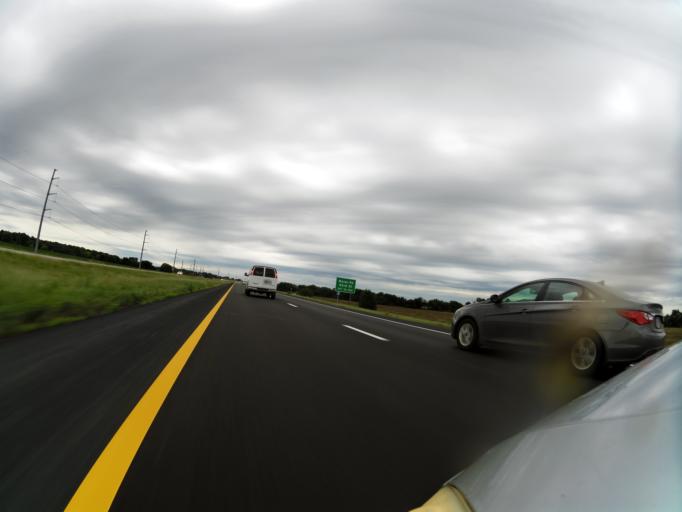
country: US
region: Kansas
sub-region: Sedgwick County
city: Maize
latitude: 37.7904
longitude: -97.4734
